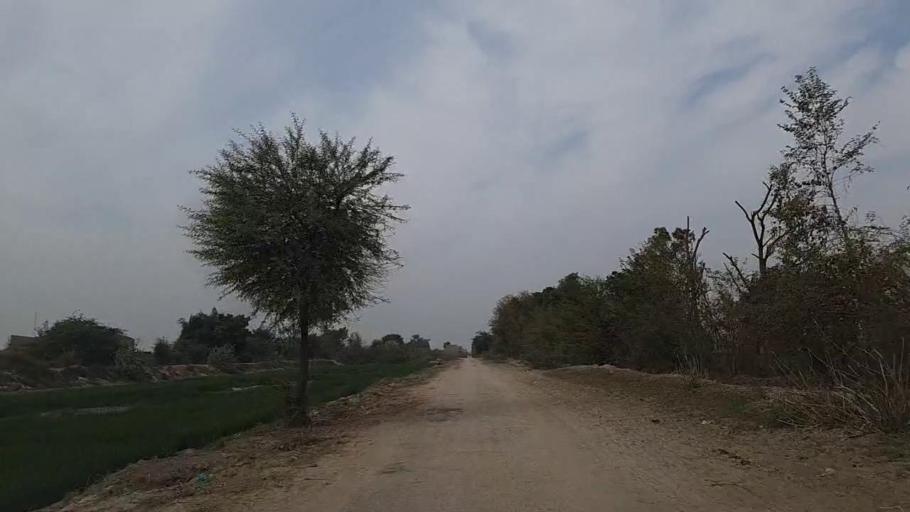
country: PK
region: Sindh
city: Daur
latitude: 26.4455
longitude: 68.4544
